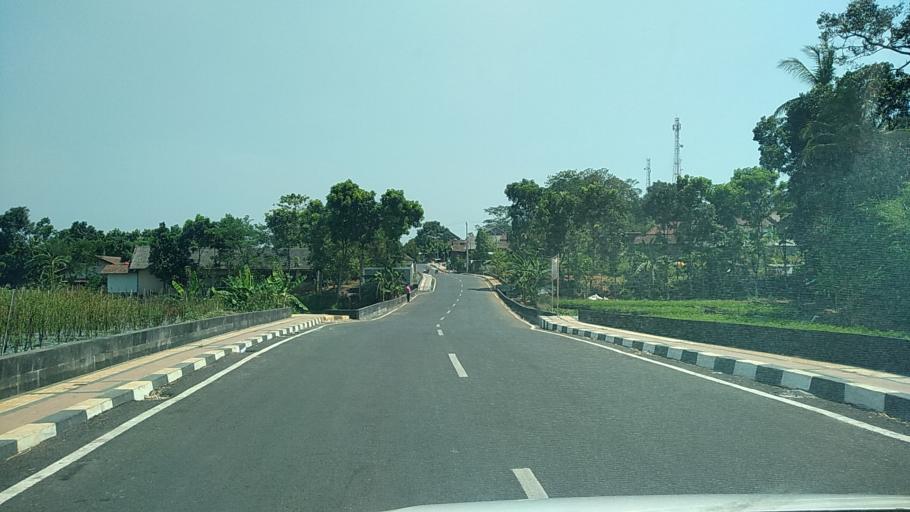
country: ID
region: Central Java
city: Ungaran
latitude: -7.0883
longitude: 110.3598
